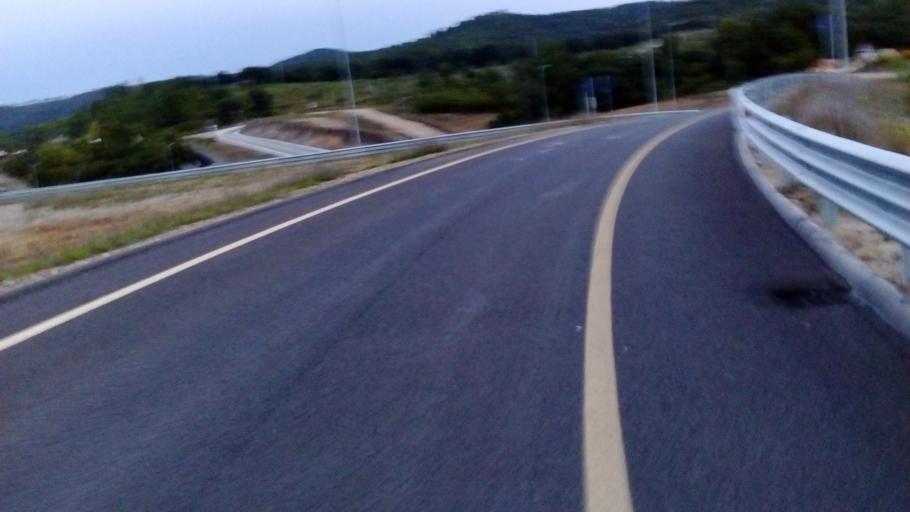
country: IT
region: Tuscany
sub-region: Provincia di Grosseto
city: Civitella Marittima
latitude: 43.0254
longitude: 11.2802
